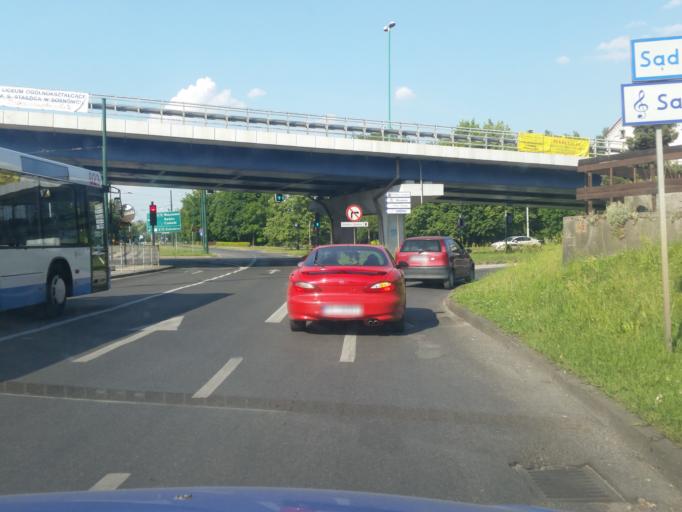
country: PL
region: Silesian Voivodeship
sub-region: Sosnowiec
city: Sosnowiec
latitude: 50.2812
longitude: 19.1356
